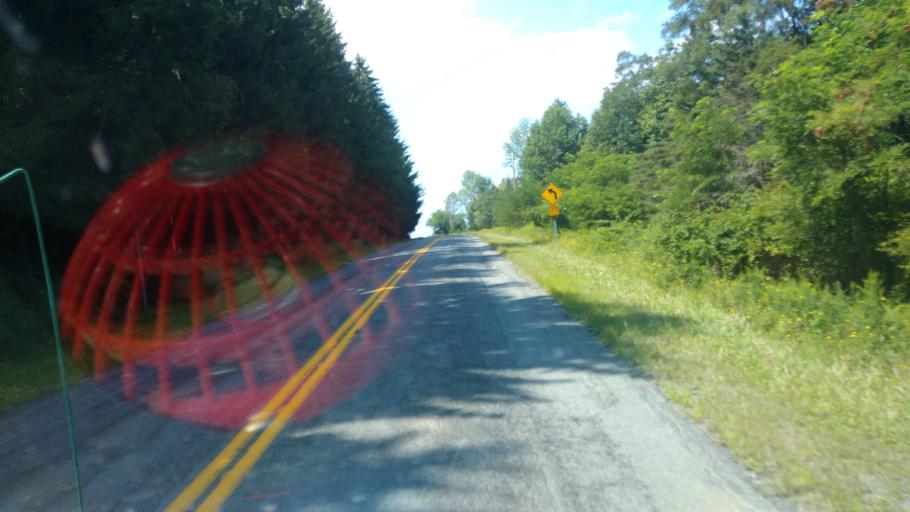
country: US
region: New York
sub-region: Steuben County
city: Canisteo
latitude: 42.3527
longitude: -77.5533
